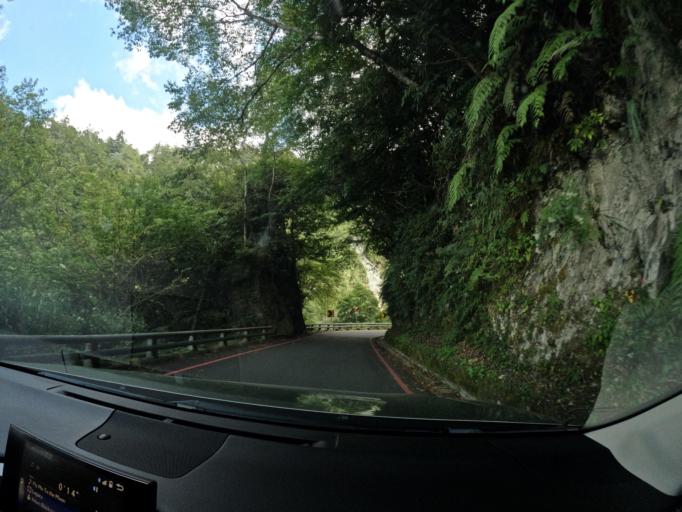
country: TW
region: Taiwan
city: Yujing
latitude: 23.2596
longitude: 120.9187
